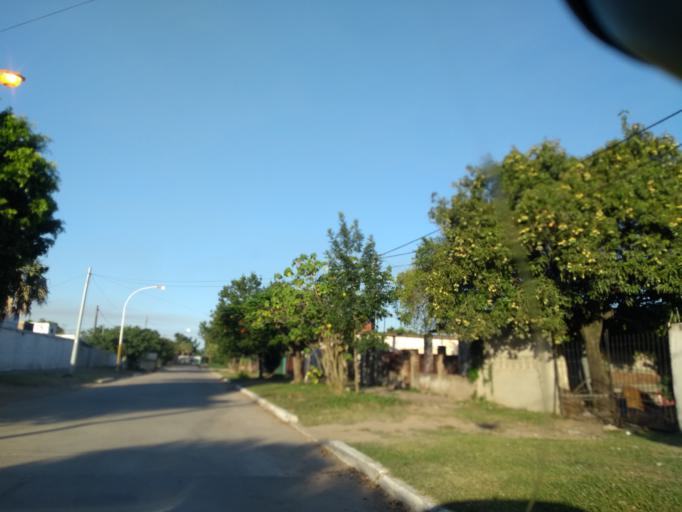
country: AR
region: Chaco
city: Barranqueras
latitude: -27.4806
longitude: -58.9461
